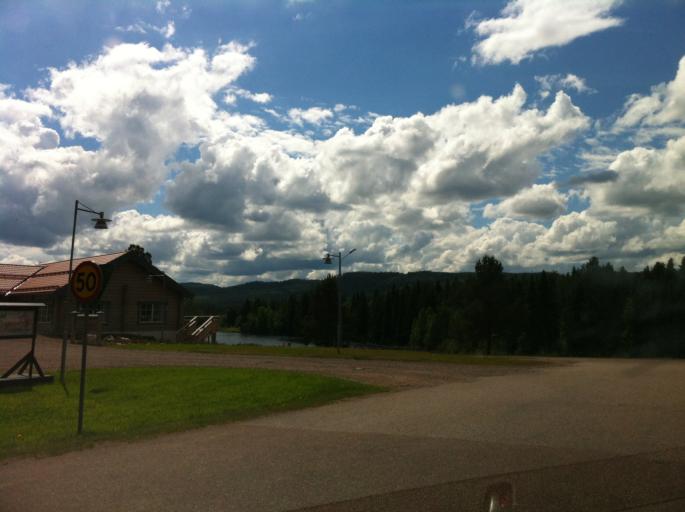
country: SE
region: Dalarna
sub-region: Malung-Saelens kommun
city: Malung
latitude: 60.8990
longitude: 13.3880
